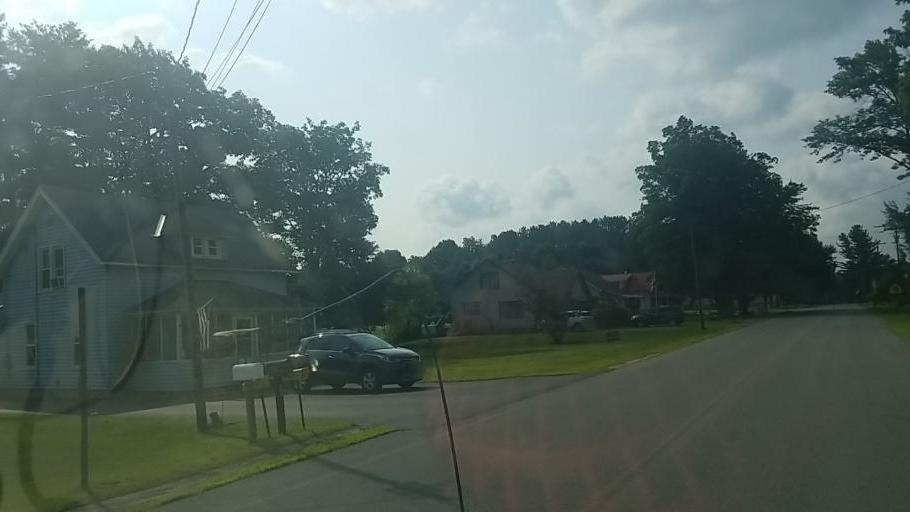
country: US
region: New York
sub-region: Fulton County
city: Broadalbin
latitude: 43.1115
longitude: -74.2636
